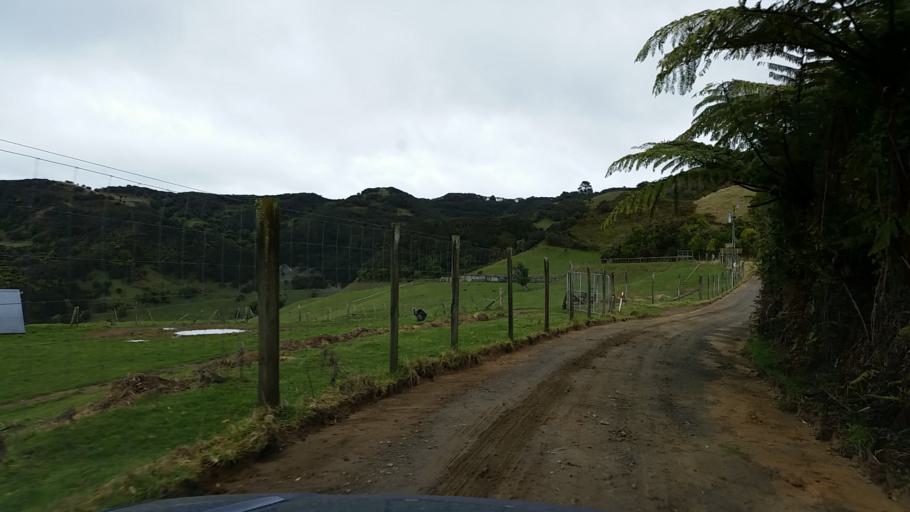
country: NZ
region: Taranaki
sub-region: South Taranaki District
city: Eltham
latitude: -39.4388
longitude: 174.6419
